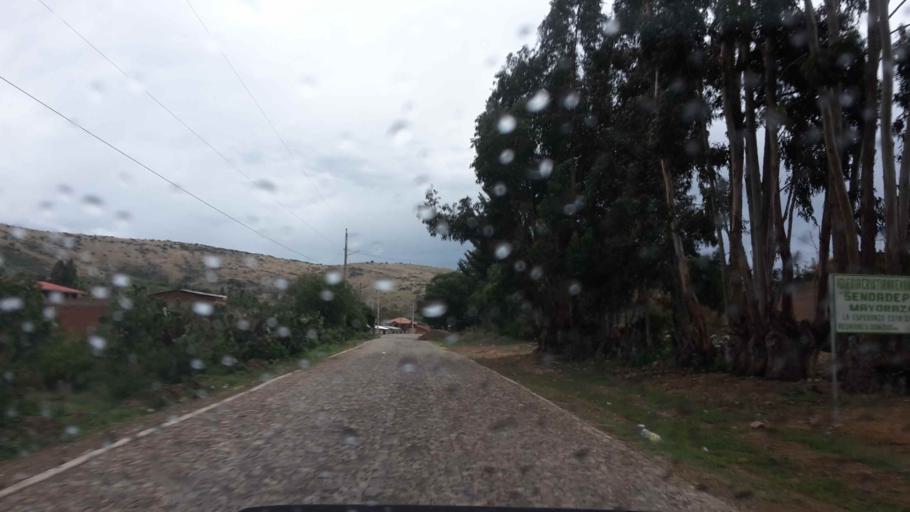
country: BO
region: Cochabamba
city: Cochabamba
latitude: -17.5497
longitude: -66.1740
